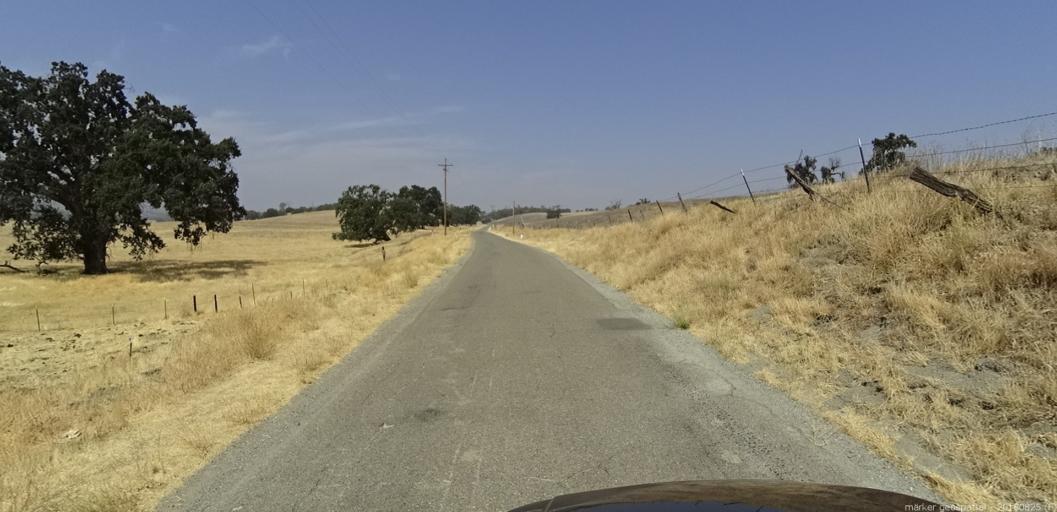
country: US
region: California
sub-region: San Luis Obispo County
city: Shandon
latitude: 35.8533
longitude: -120.3863
